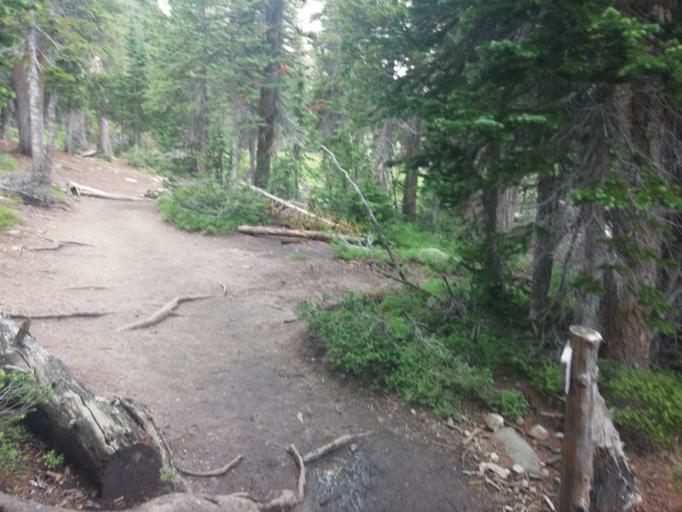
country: US
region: Colorado
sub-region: Boulder County
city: Nederland
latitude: 40.0864
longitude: -105.5942
